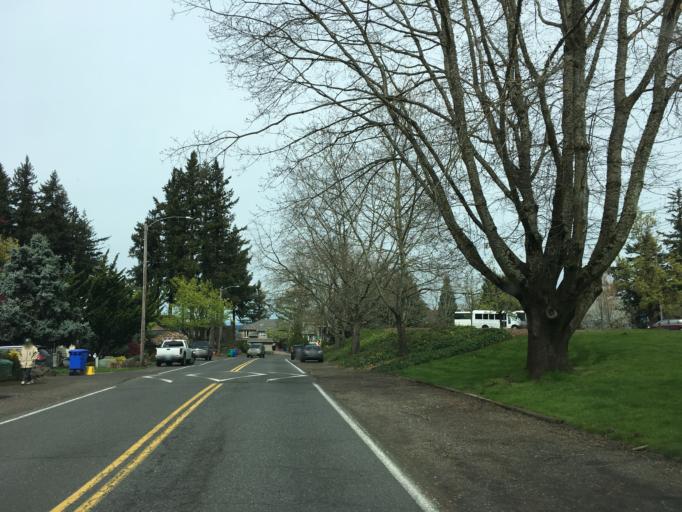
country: US
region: Oregon
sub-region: Multnomah County
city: Lents
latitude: 45.5509
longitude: -122.5691
